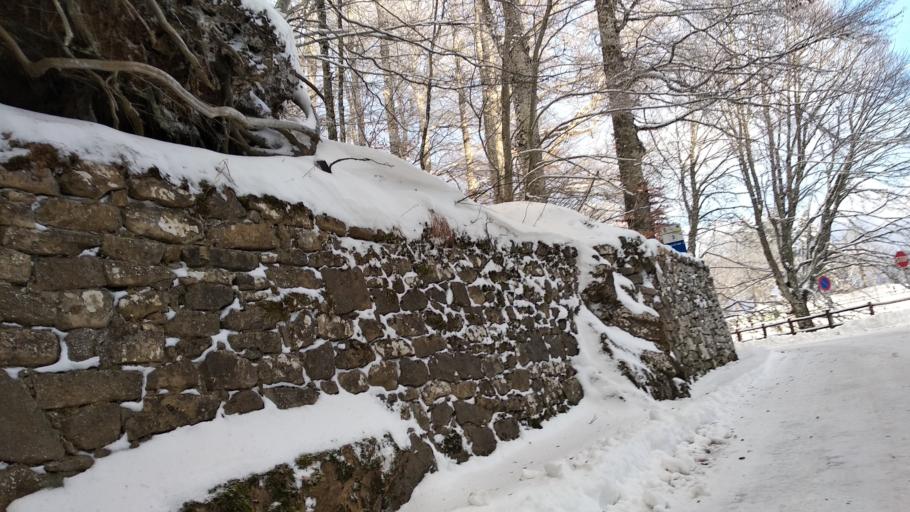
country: IT
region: Tuscany
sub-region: Province of Arezzo
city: Chiusi della Verna
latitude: 43.7076
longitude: 11.9358
